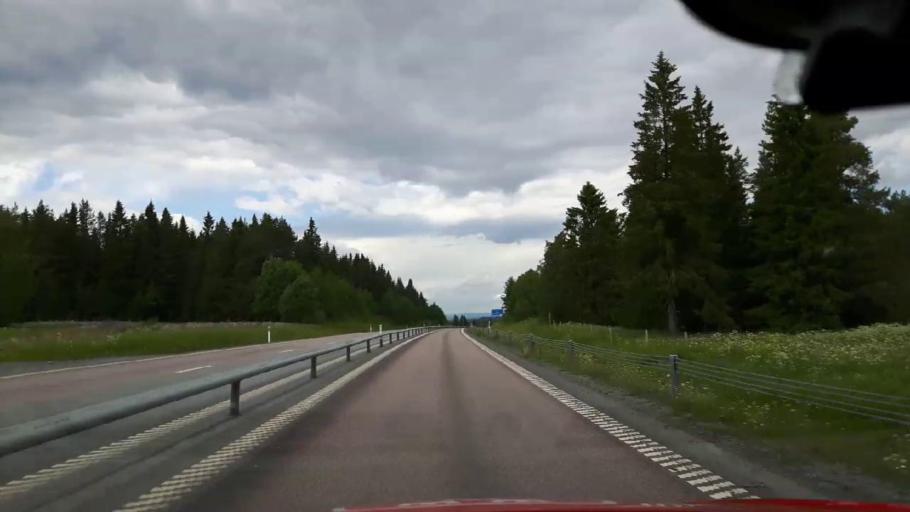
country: SE
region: Jaemtland
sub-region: Krokoms Kommun
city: Krokom
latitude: 63.2629
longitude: 14.5455
